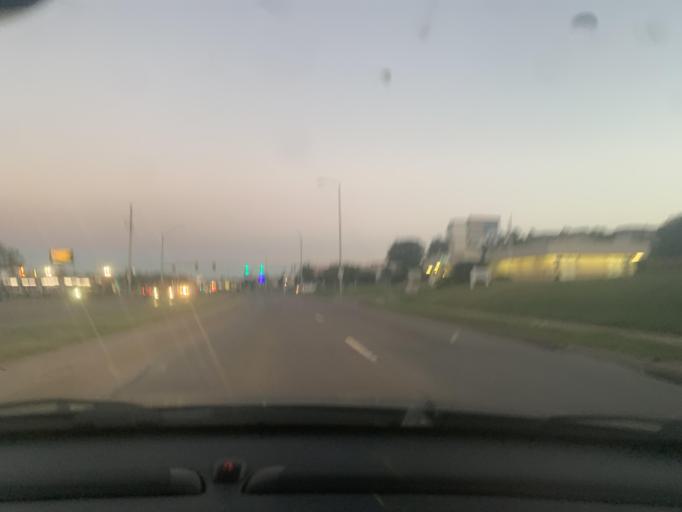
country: US
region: Nebraska
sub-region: Douglas County
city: Ralston
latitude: 41.2923
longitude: -96.0532
